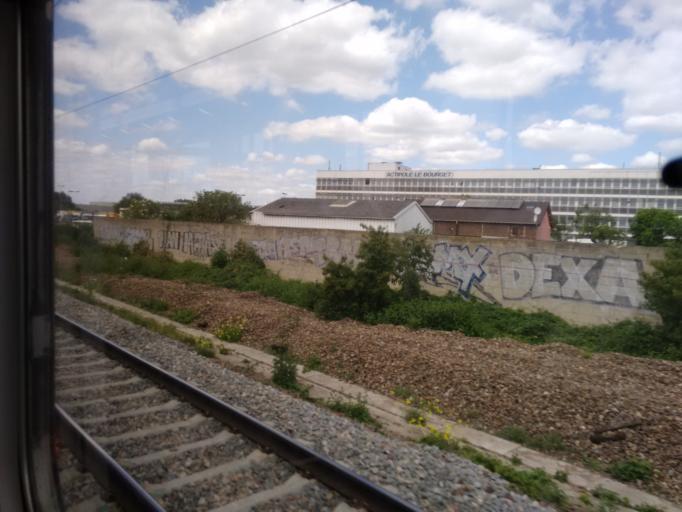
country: FR
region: Ile-de-France
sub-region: Departement de Seine-Saint-Denis
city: Le Bourget
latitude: 48.9329
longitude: 2.4424
